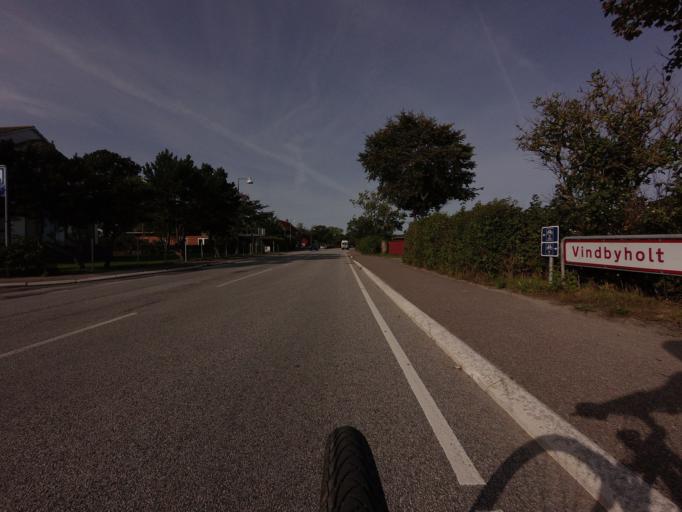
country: DK
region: Zealand
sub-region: Faxe Kommune
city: Fakse Ladeplads
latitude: 55.2078
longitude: 12.1501
